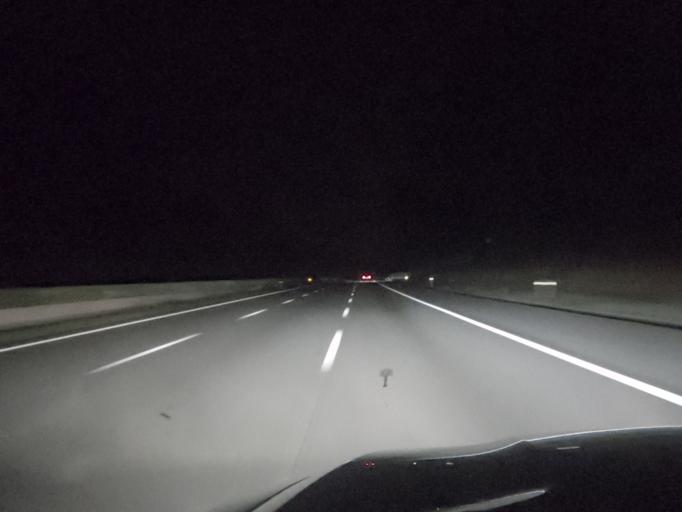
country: PT
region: Aveiro
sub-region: Estarreja
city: Avanca
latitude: 40.8205
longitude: -8.5511
